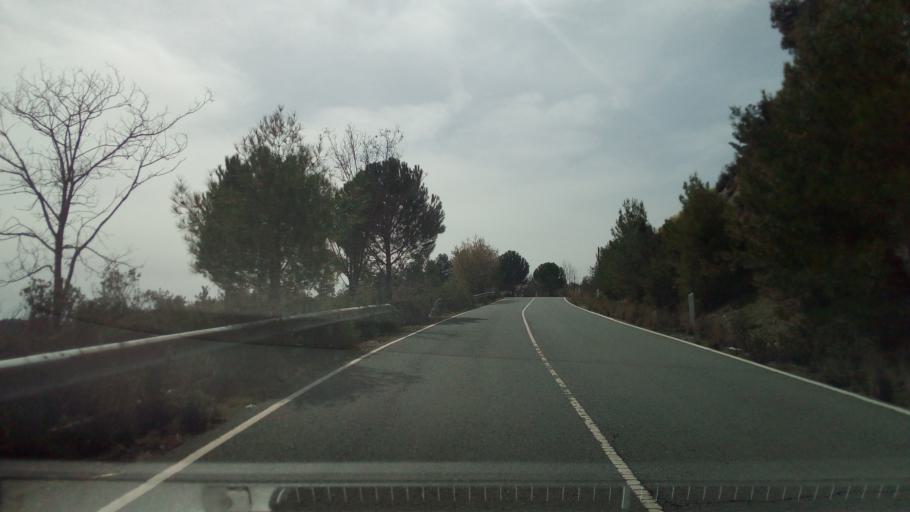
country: CY
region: Limassol
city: Pelendri
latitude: 34.9015
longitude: 32.9862
